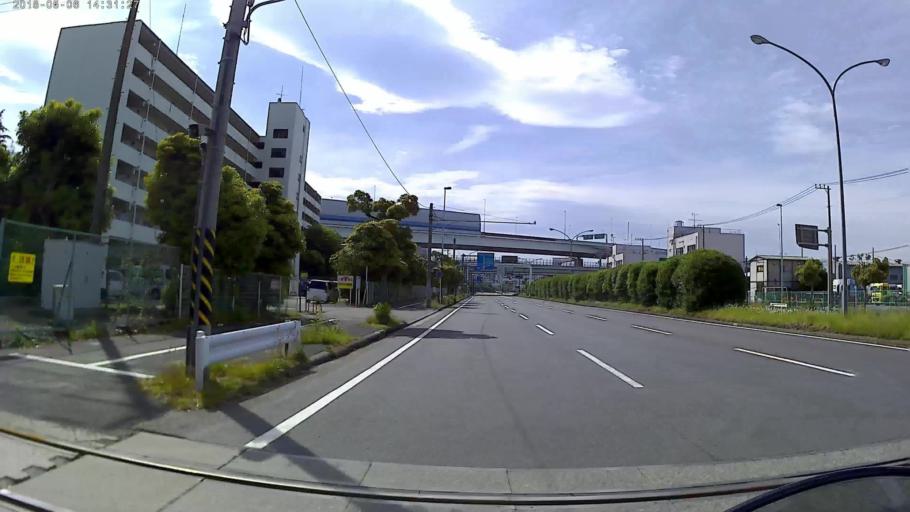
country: JP
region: Kanagawa
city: Yokohama
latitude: 35.4303
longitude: 139.6728
